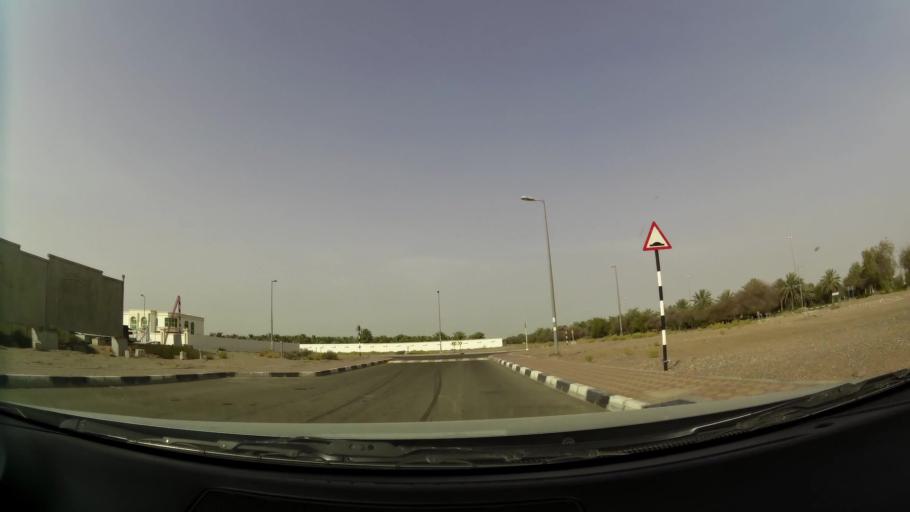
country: AE
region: Abu Dhabi
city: Al Ain
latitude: 24.1938
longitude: 55.6179
